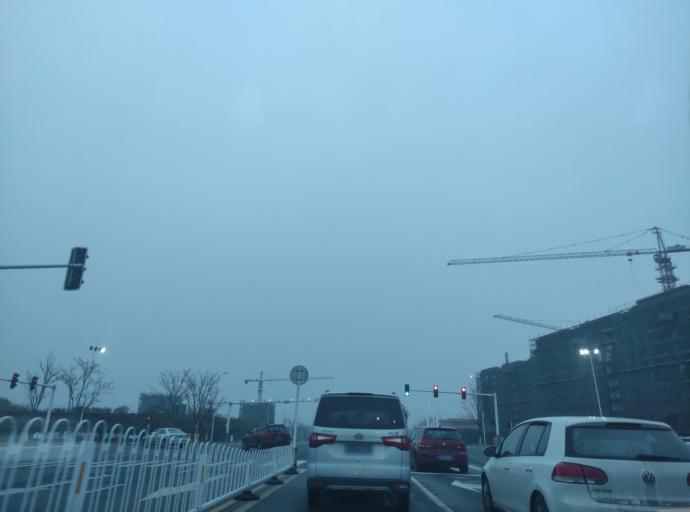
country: CN
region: Jiangxi Sheng
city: Pingxiang
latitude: 27.6716
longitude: 113.8531
